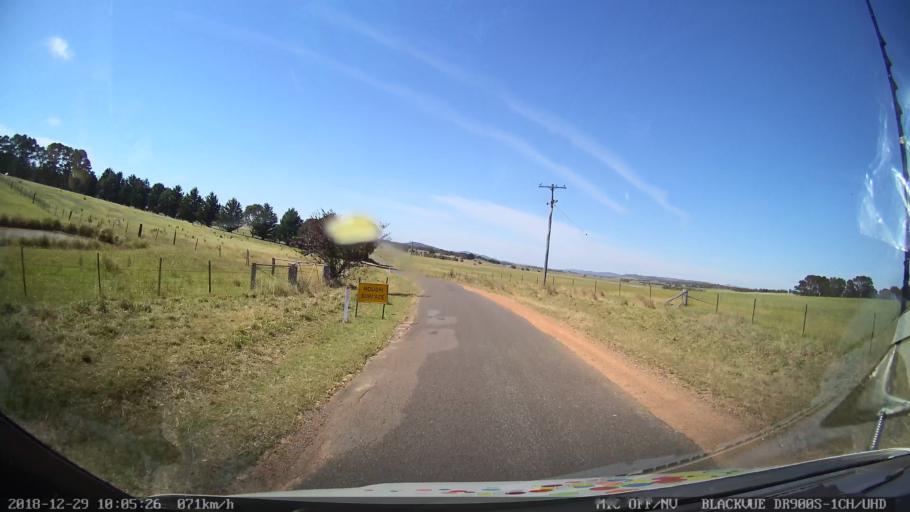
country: AU
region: New South Wales
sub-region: Goulburn Mulwaree
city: Goulburn
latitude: -34.8331
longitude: 149.4532
